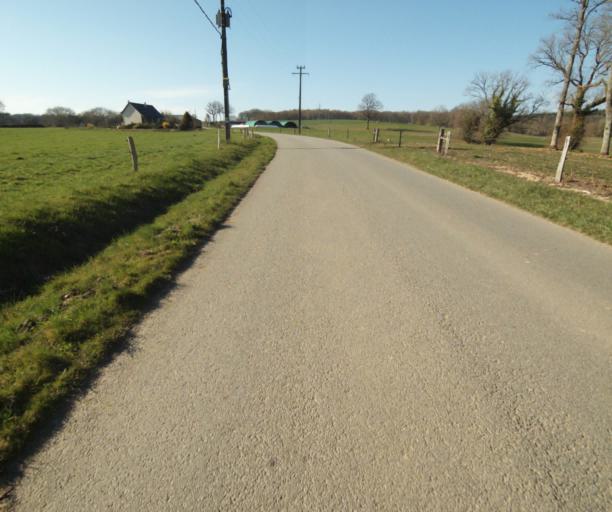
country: FR
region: Limousin
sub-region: Departement de la Correze
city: Chamboulive
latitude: 45.4716
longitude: 1.7213
